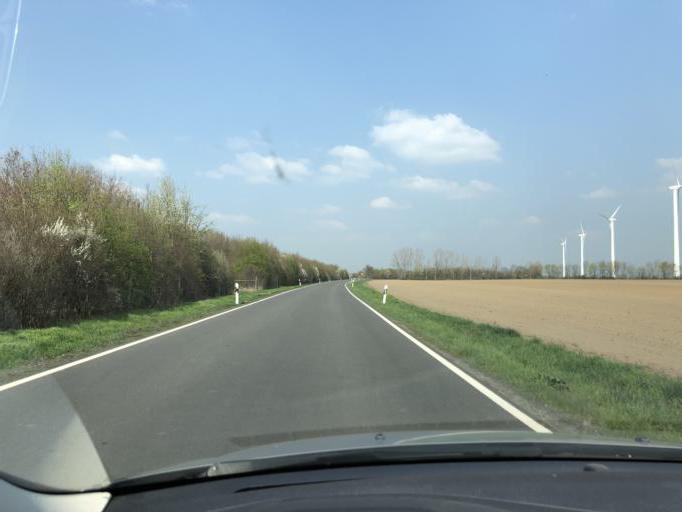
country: DE
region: Saxony
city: Wiedemar
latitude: 51.4775
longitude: 12.2265
